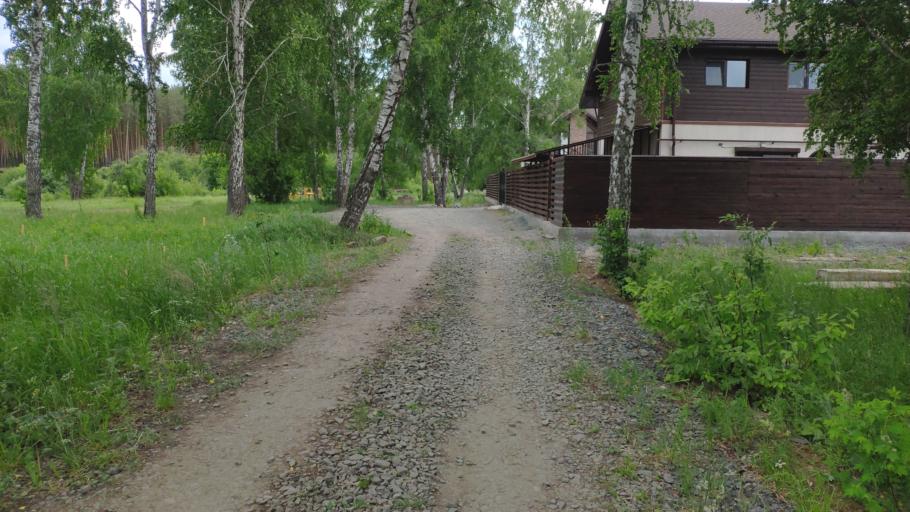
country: RU
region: Bashkortostan
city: Abzakovo
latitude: 53.8129
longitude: 58.6375
